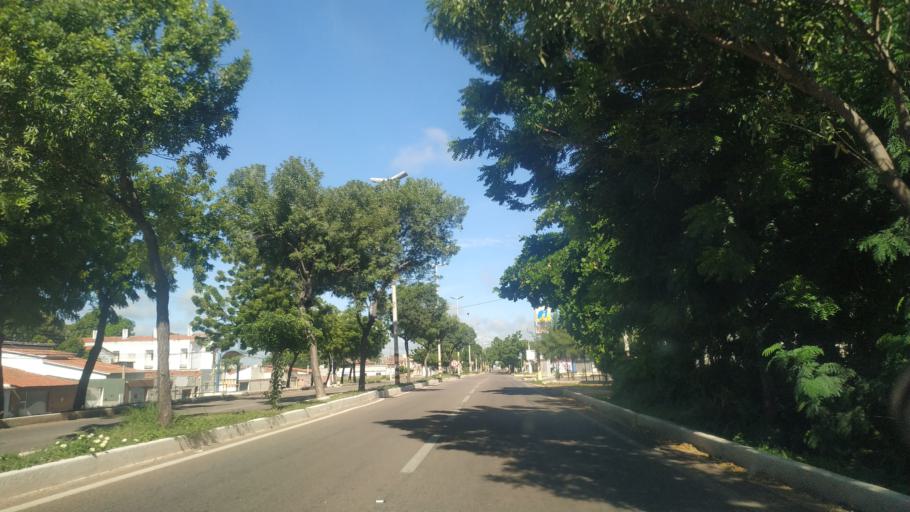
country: BR
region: Rio Grande do Norte
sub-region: Mossoro
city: Mossoro
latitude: -5.1920
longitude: -37.3659
